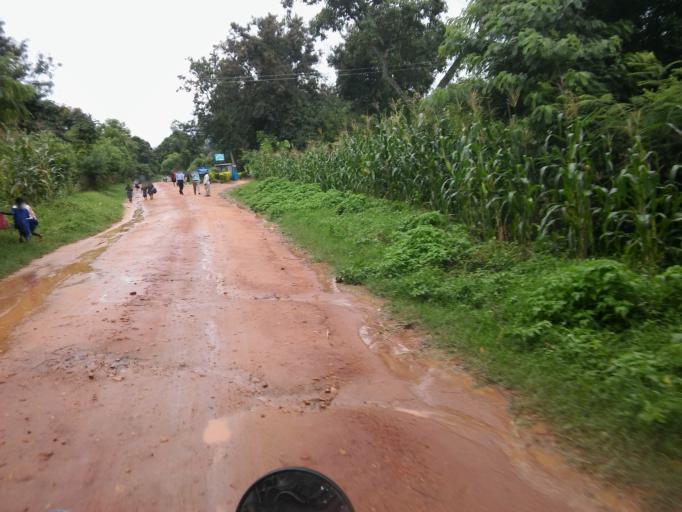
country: UG
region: Eastern Region
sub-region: Mbale District
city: Mbale
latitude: 0.9858
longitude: 34.2158
